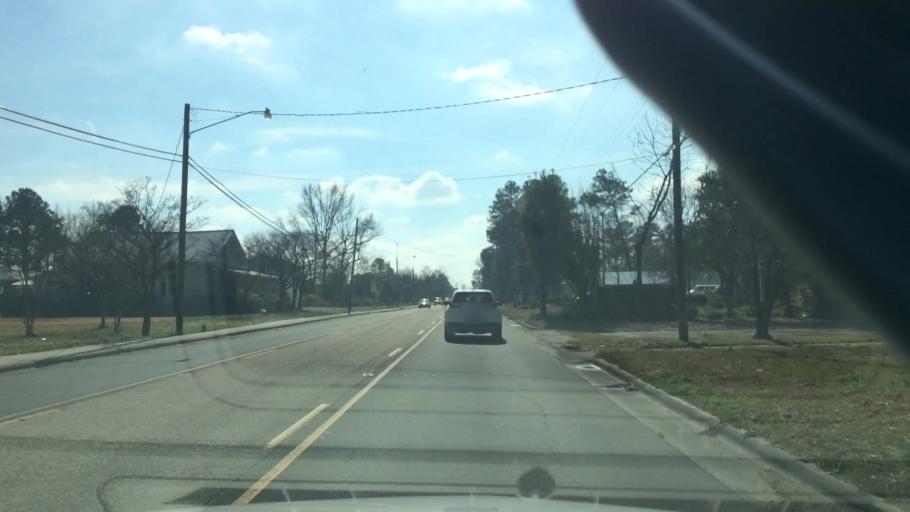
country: US
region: North Carolina
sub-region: Duplin County
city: Beulaville
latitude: 34.9217
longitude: -77.7742
